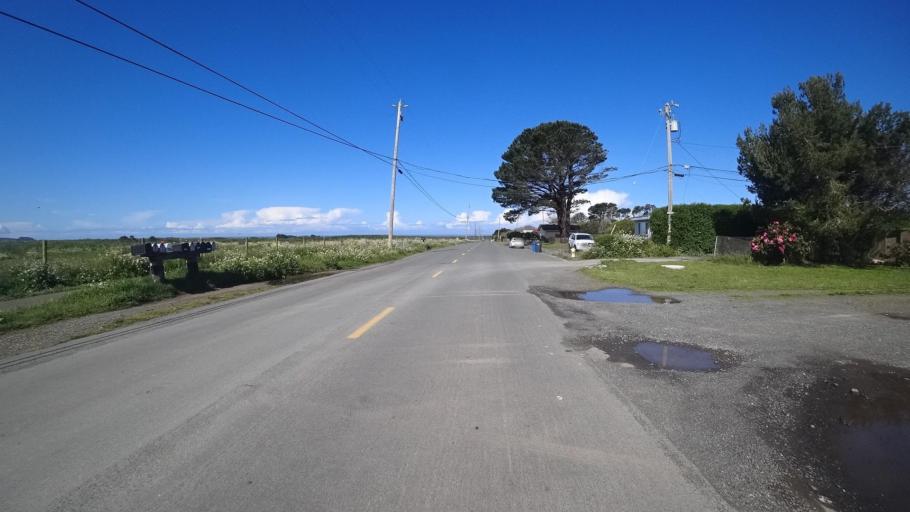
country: US
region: California
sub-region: Humboldt County
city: McKinleyville
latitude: 40.9339
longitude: -124.1221
